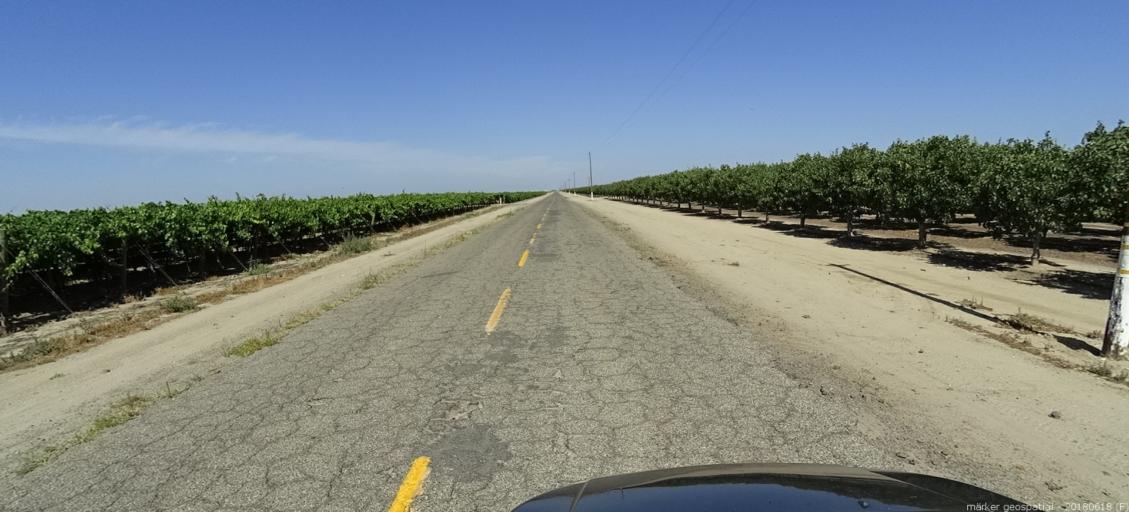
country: US
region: California
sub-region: Fresno County
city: Mendota
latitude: 36.8366
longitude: -120.2399
